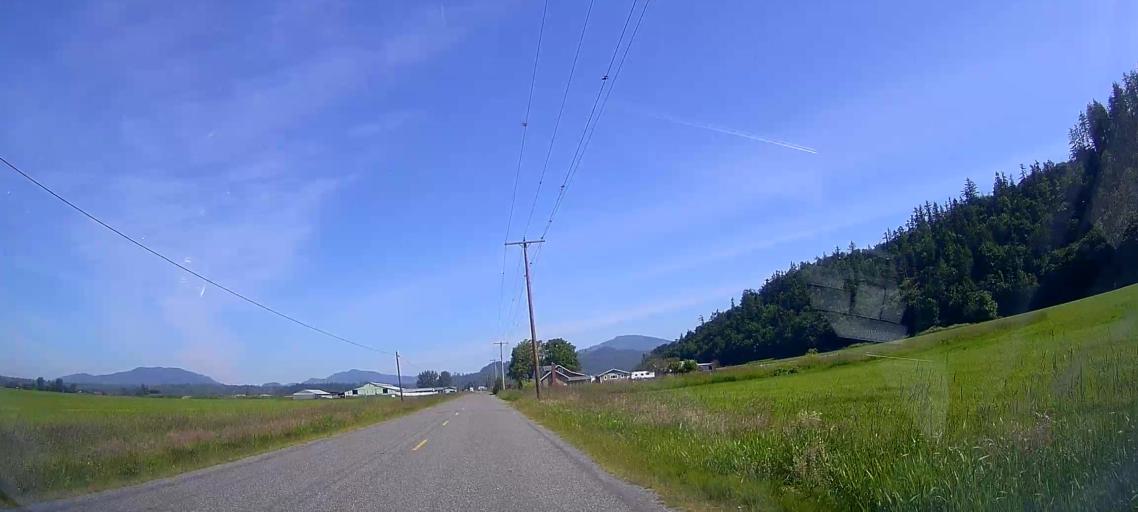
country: US
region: Washington
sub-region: Skagit County
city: Burlington
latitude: 48.4960
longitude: -122.3076
